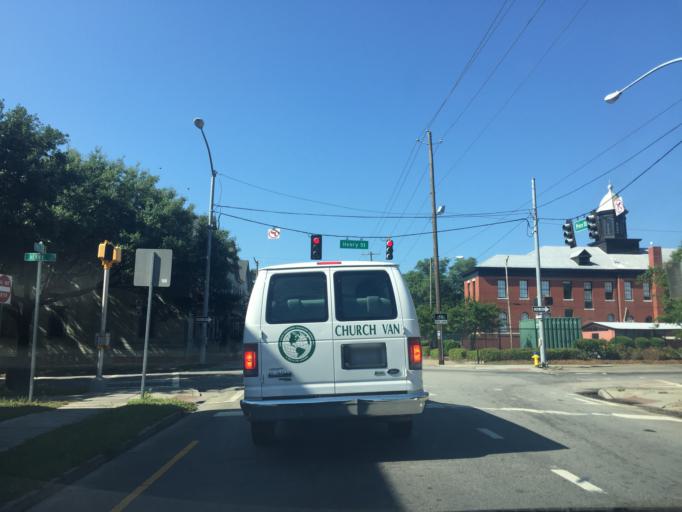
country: US
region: Georgia
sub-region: Chatham County
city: Savannah
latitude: 32.0621
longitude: -81.0925
